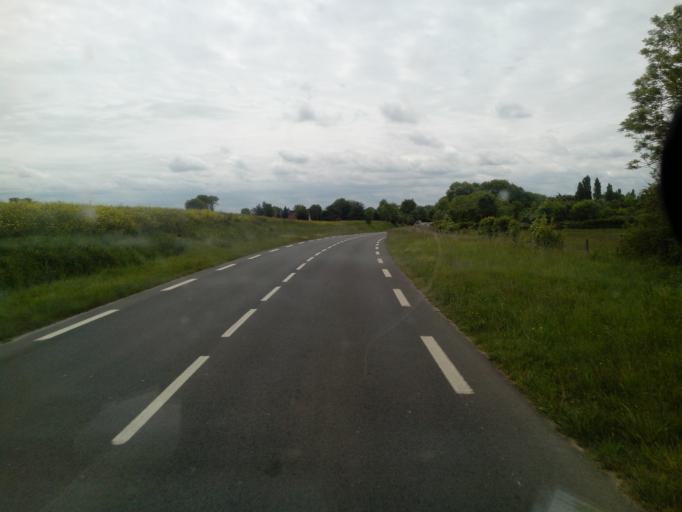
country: FR
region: Lower Normandy
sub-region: Departement du Calvados
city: Amfreville
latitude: 49.2534
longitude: -0.2426
